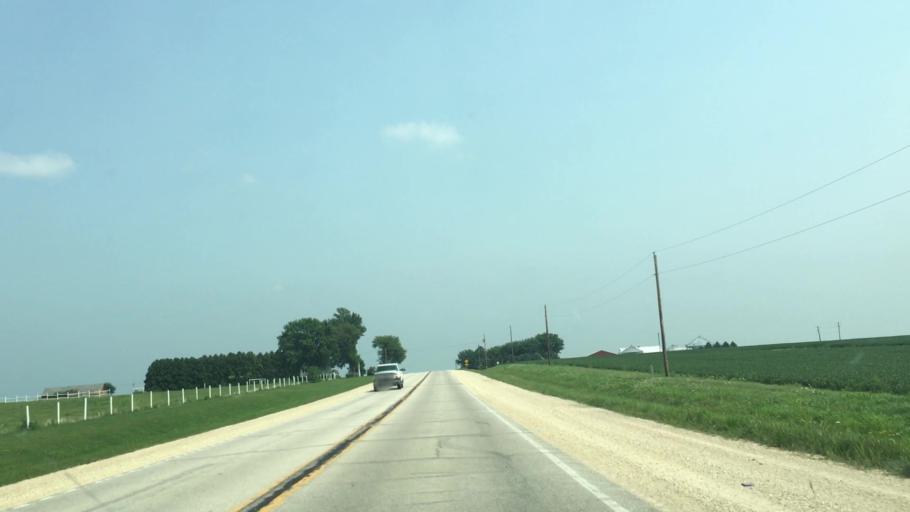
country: US
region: Iowa
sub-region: Fayette County
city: Oelwein
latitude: 42.6796
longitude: -91.8683
